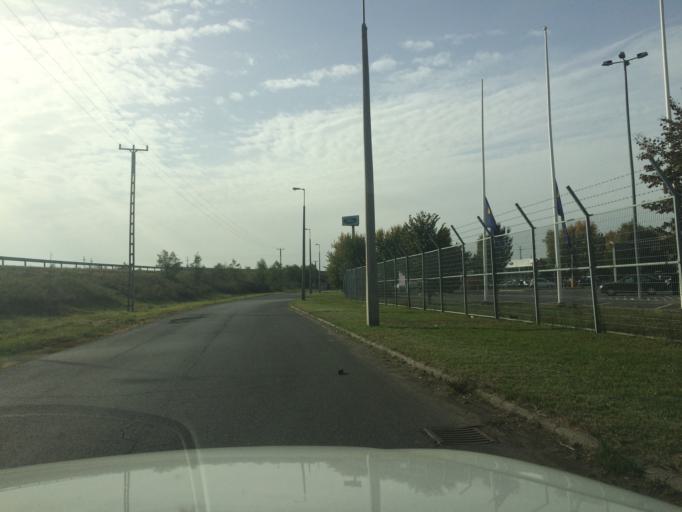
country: HU
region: Szabolcs-Szatmar-Bereg
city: Nyiregyhaza
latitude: 47.9177
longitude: 21.7191
